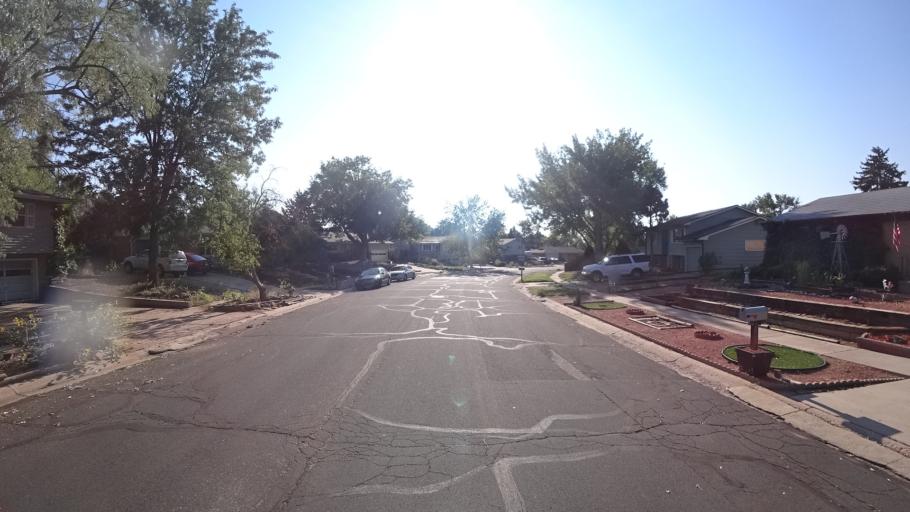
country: US
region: Colorado
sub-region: El Paso County
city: Colorado Springs
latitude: 38.8907
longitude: -104.8377
